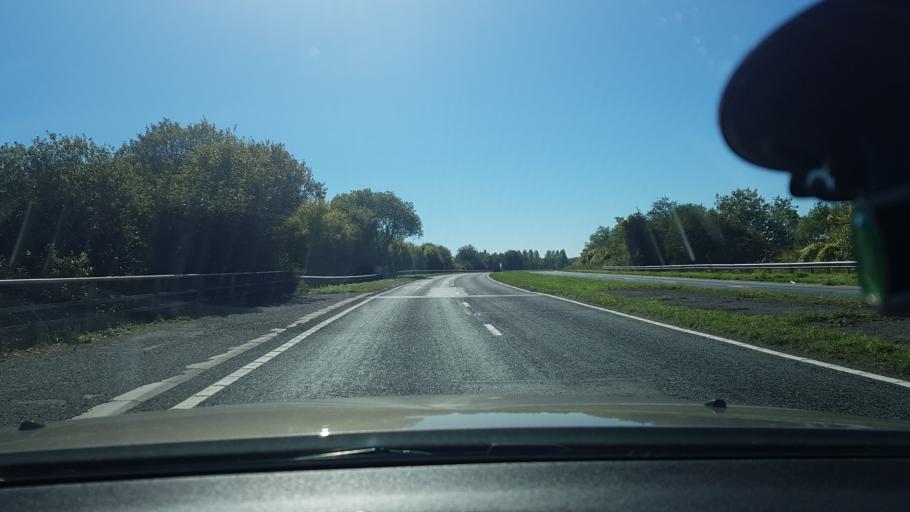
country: GB
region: England
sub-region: Hampshire
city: Alton
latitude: 51.1442
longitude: -0.9593
